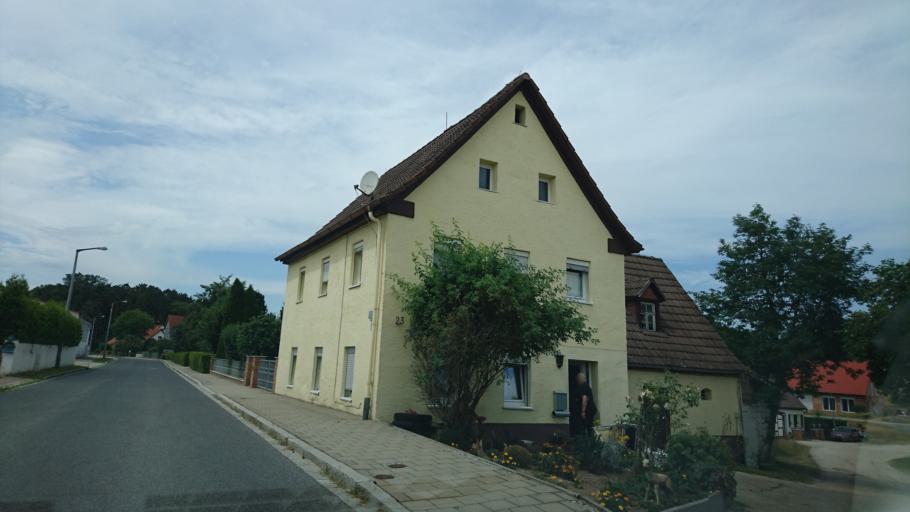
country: DE
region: Bavaria
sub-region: Regierungsbezirk Mittelfranken
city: Roth
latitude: 49.2087
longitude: 11.0886
